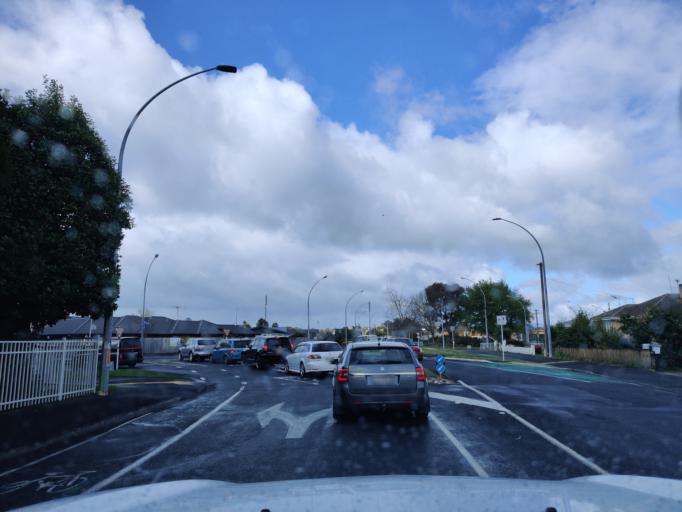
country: NZ
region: Waikato
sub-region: Hamilton City
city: Hamilton
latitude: -37.7936
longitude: 175.2485
